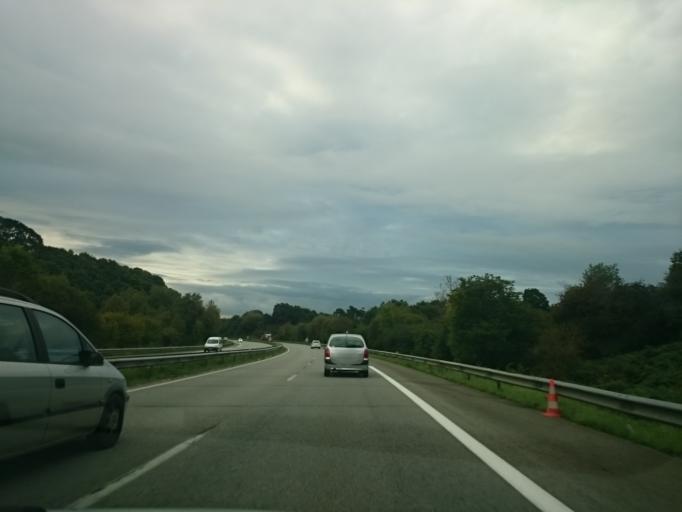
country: FR
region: Brittany
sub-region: Departement du Finistere
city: Dineault
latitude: 48.2543
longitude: -4.1150
